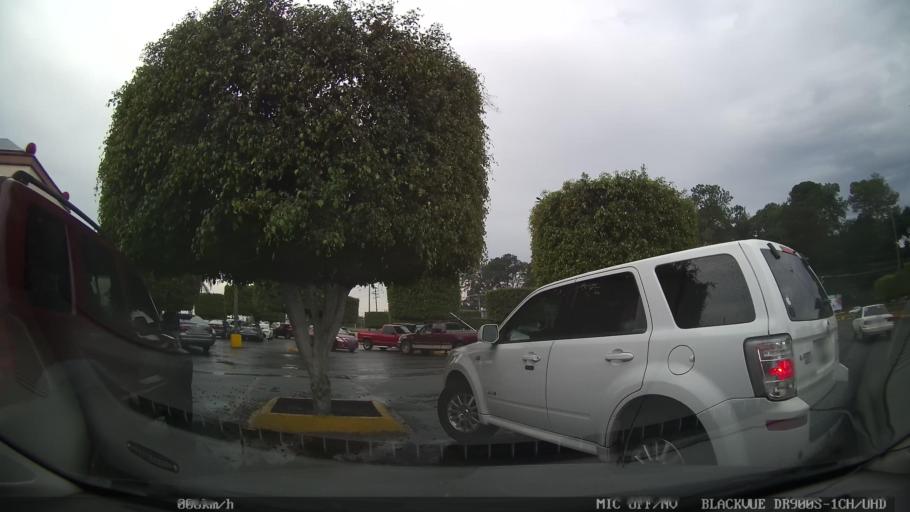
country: MX
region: Michoacan
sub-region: Uruapan
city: Santa Rosa (Santa Barbara)
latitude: 19.3833
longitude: -102.0586
